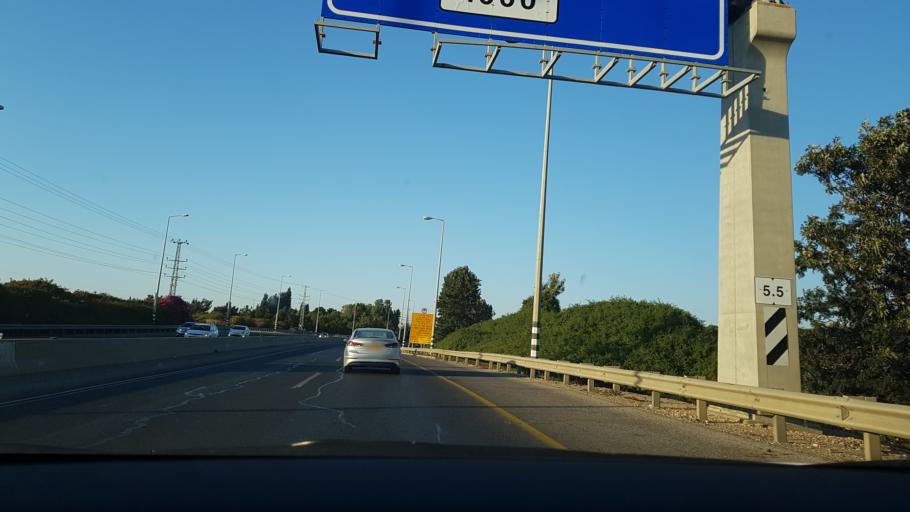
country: IL
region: Central District
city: Ness Ziona
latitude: 31.9404
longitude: 34.7799
